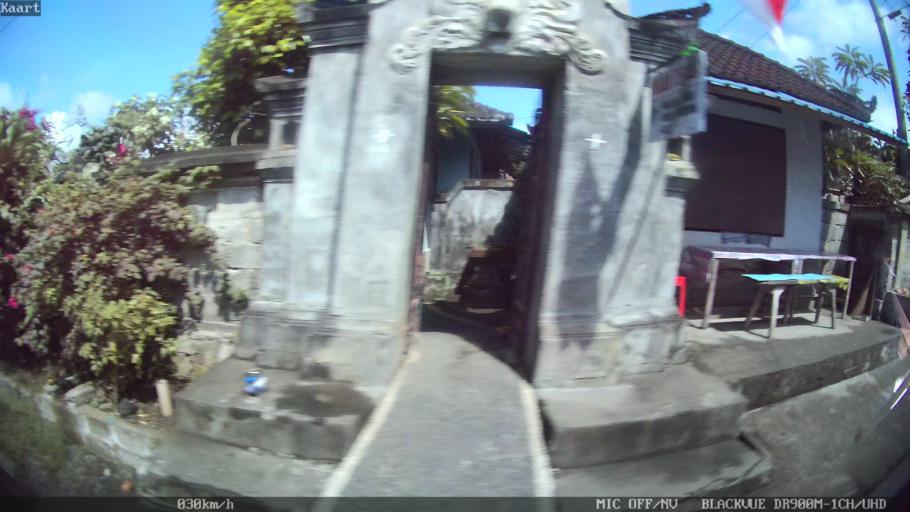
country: ID
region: Bali
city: Banjar Sedang
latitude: -8.5602
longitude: 115.2690
